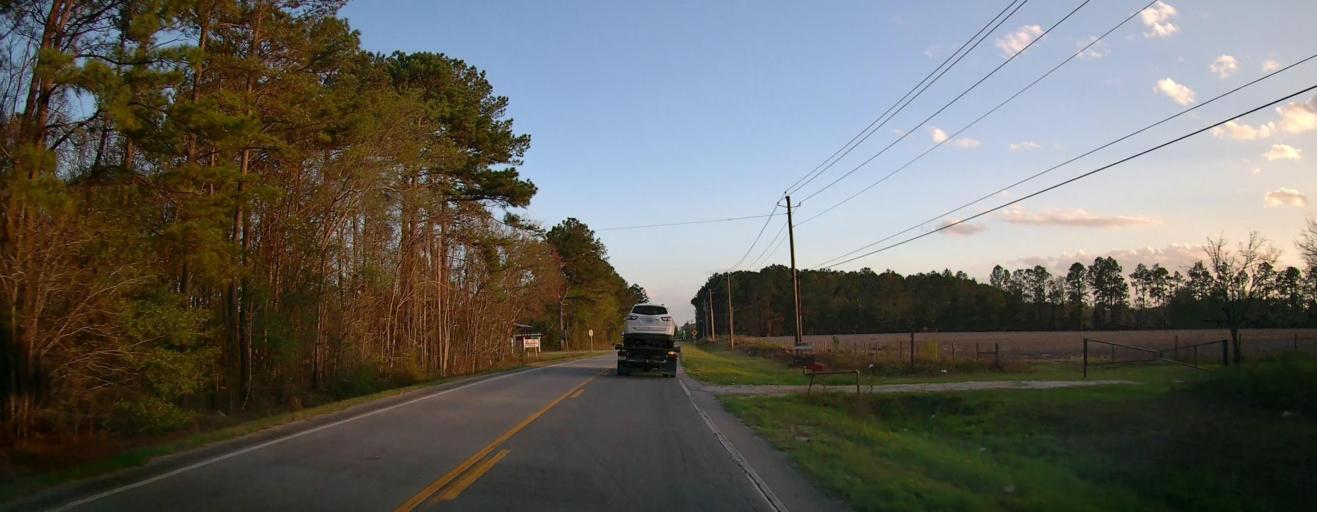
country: US
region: Georgia
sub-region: Chatham County
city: Bloomingdale
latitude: 32.1402
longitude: -81.3900
